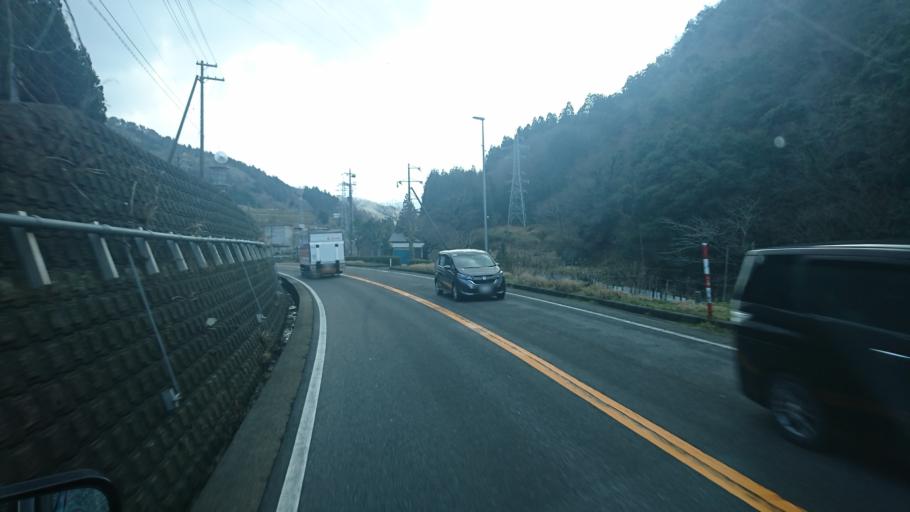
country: JP
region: Tottori
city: Tottori
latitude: 35.5439
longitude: 134.5047
